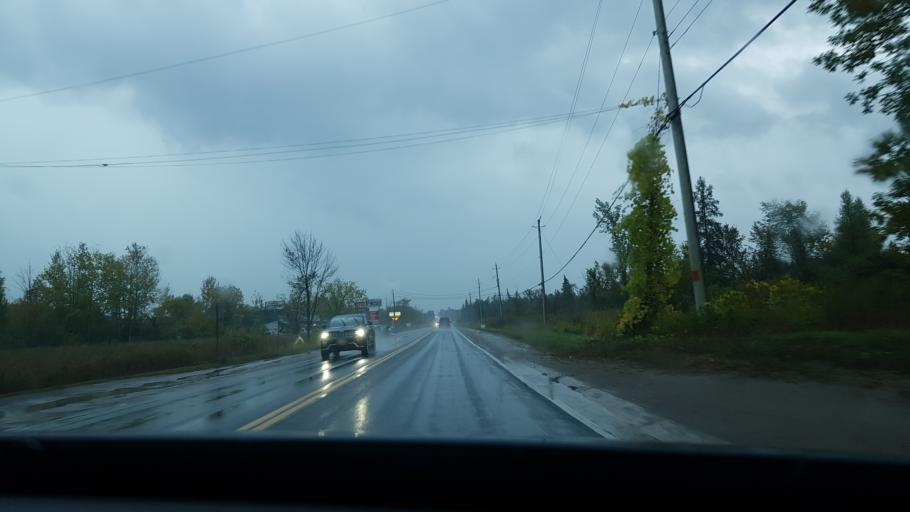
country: CA
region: Ontario
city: Peterborough
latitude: 44.3683
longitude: -78.3811
